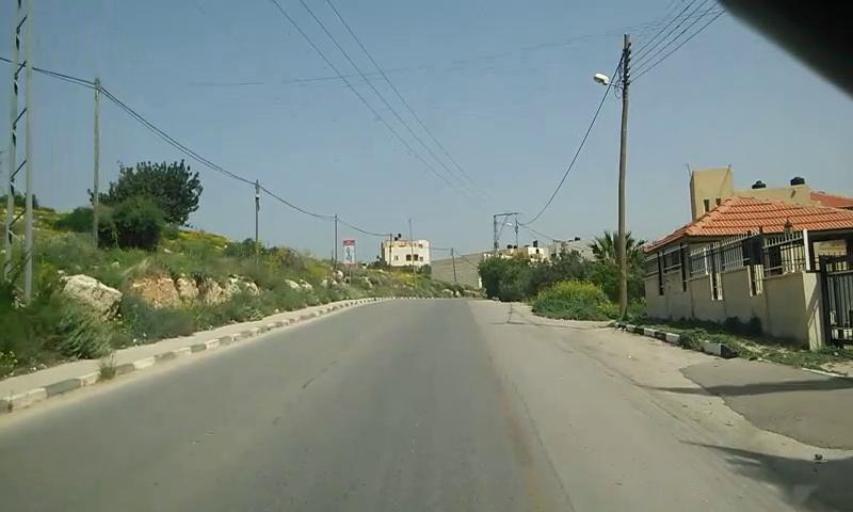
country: PS
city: Al Badhan
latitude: 32.2614
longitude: 35.3270
